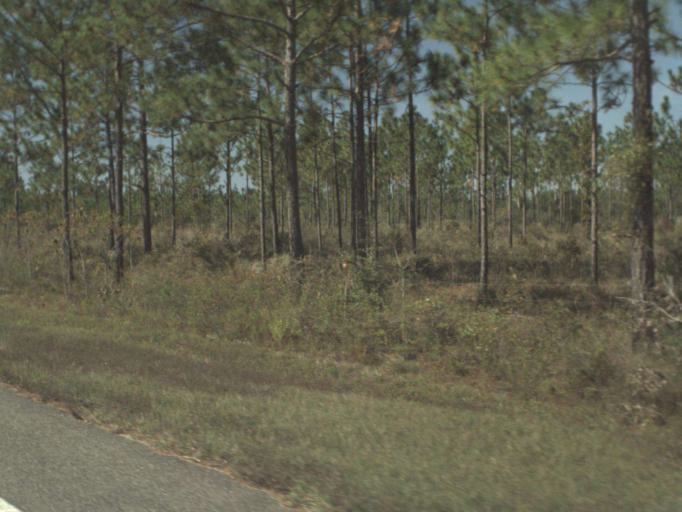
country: US
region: Florida
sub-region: Liberty County
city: Bristol
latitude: 30.4705
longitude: -84.9377
